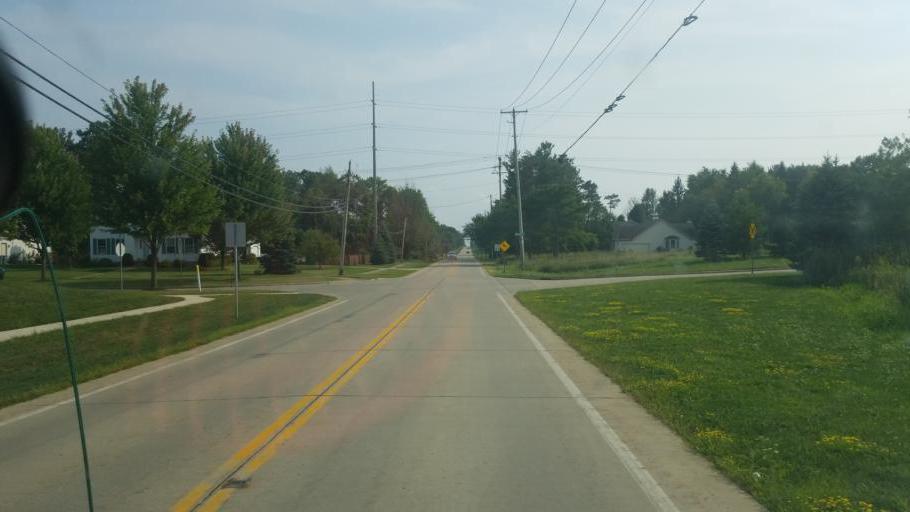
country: US
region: Ohio
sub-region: Medina County
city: Medina
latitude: 41.1209
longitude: -81.8840
